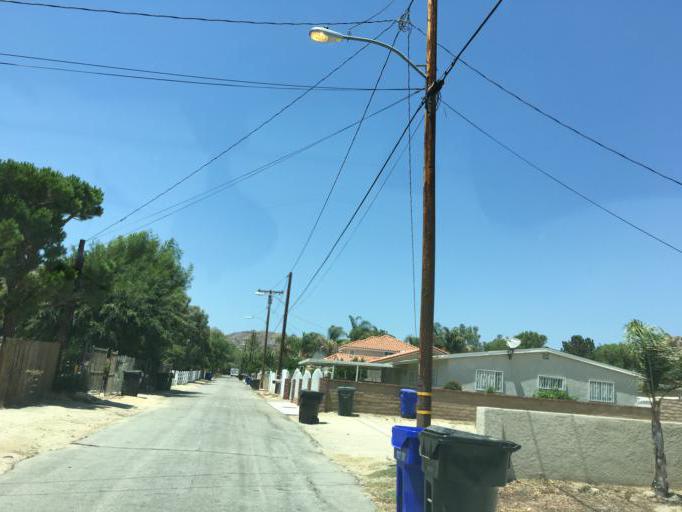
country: US
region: California
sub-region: Los Angeles County
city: Val Verde
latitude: 34.4475
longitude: -118.6678
